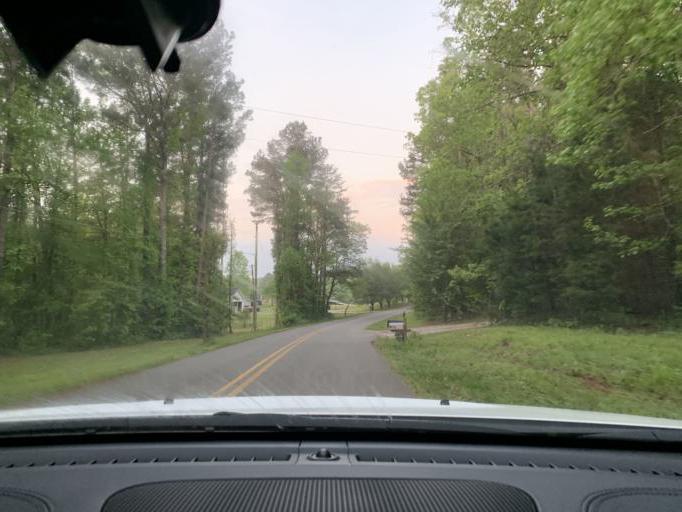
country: US
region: Georgia
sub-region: Dawson County
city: Dawsonville
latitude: 34.3308
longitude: -84.1730
